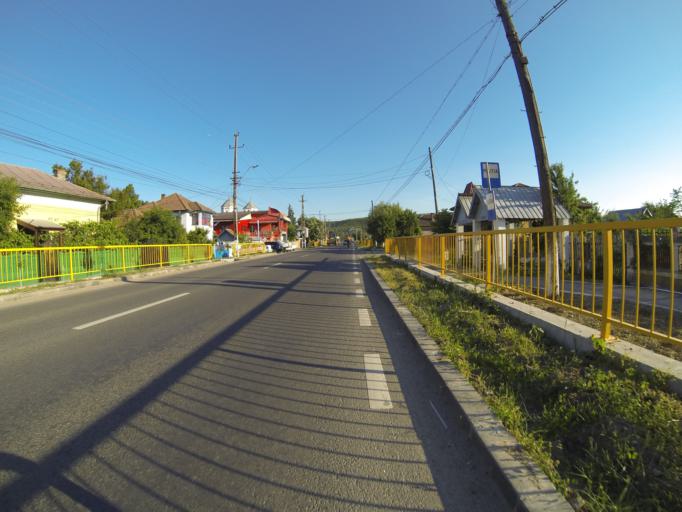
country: RO
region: Dolj
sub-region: Comuna Podari
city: Podari
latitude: 44.2476
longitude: 23.7799
